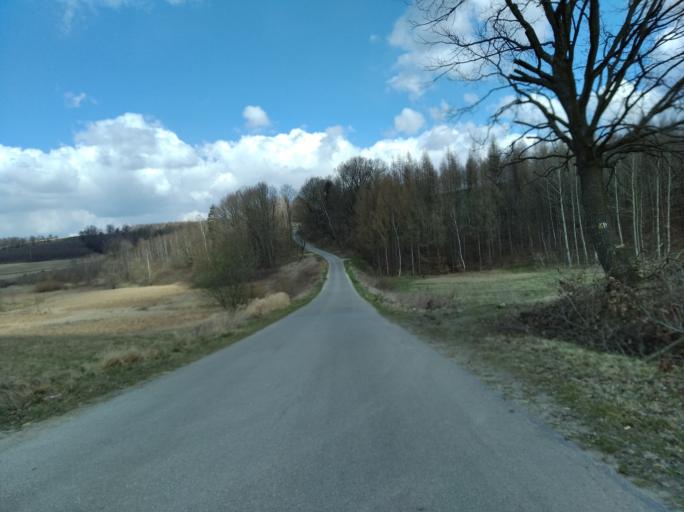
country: PL
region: Subcarpathian Voivodeship
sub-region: Powiat strzyzowski
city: Wisniowa
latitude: 49.9214
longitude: 21.7025
